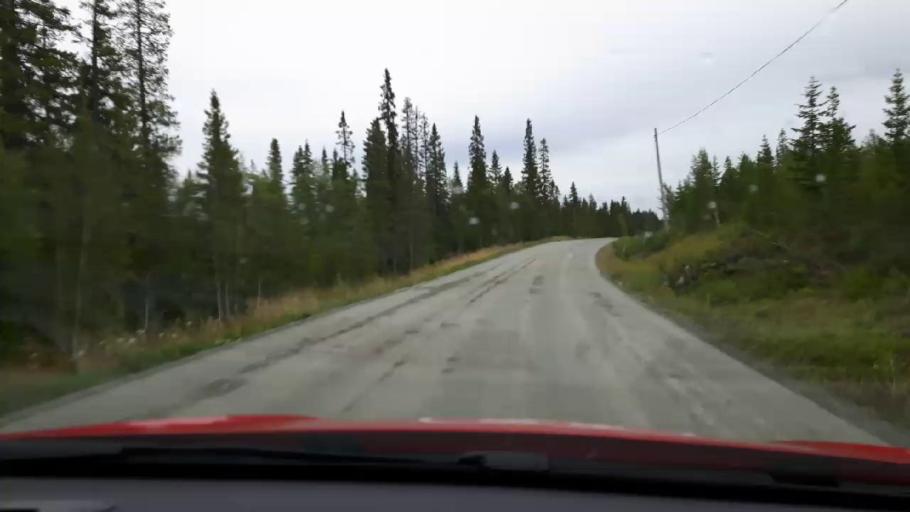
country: SE
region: Jaemtland
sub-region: Are Kommun
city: Jarpen
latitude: 63.4263
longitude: 13.3393
